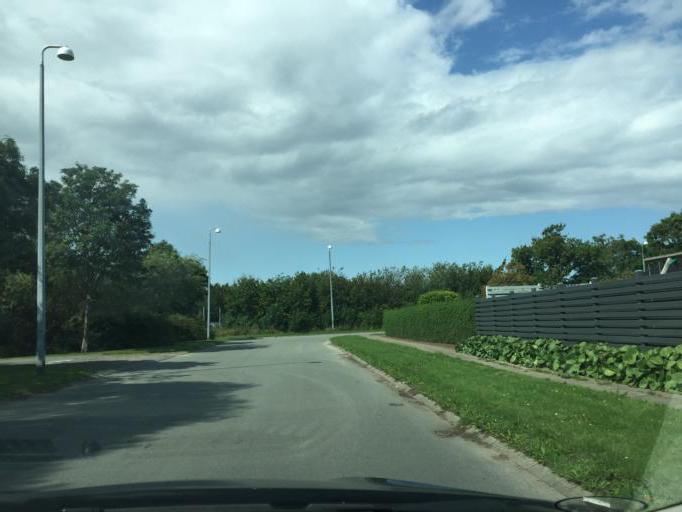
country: DK
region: South Denmark
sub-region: Odense Kommune
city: Neder Holluf
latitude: 55.3668
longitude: 10.4493
